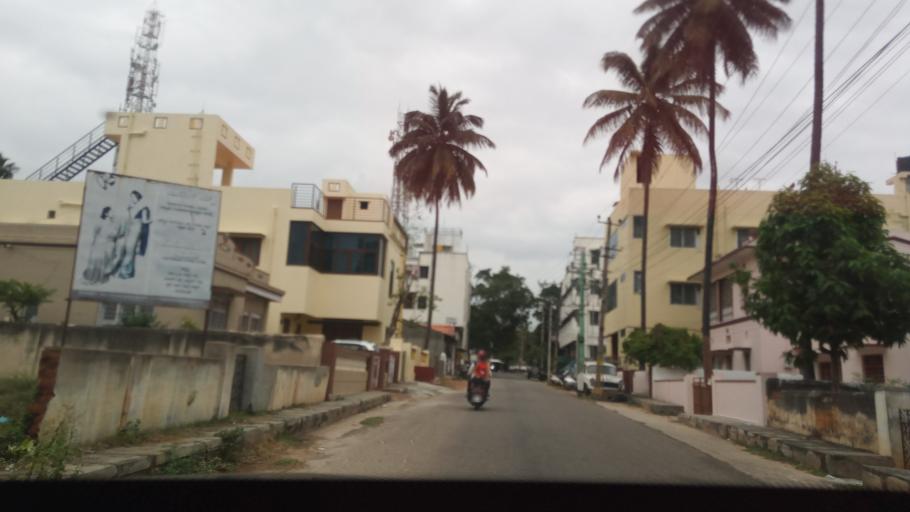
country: IN
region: Karnataka
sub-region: Mysore
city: Mysore
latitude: 12.3021
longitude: 76.6341
